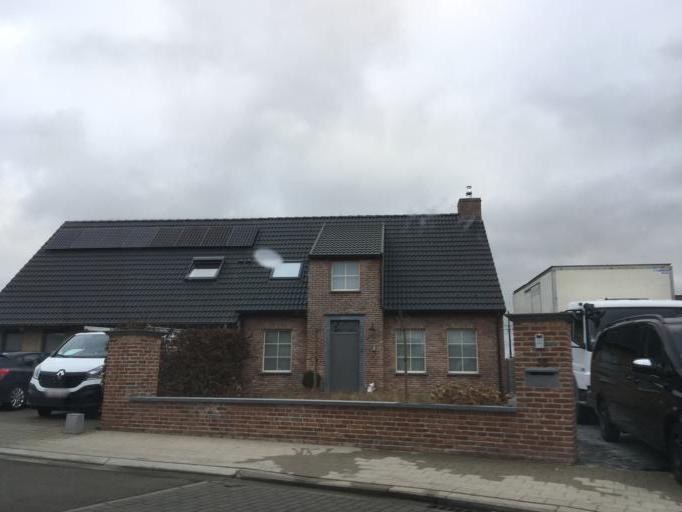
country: BE
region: Flanders
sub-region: Provincie West-Vlaanderen
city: Roeselare
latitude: 50.9645
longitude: 3.1159
